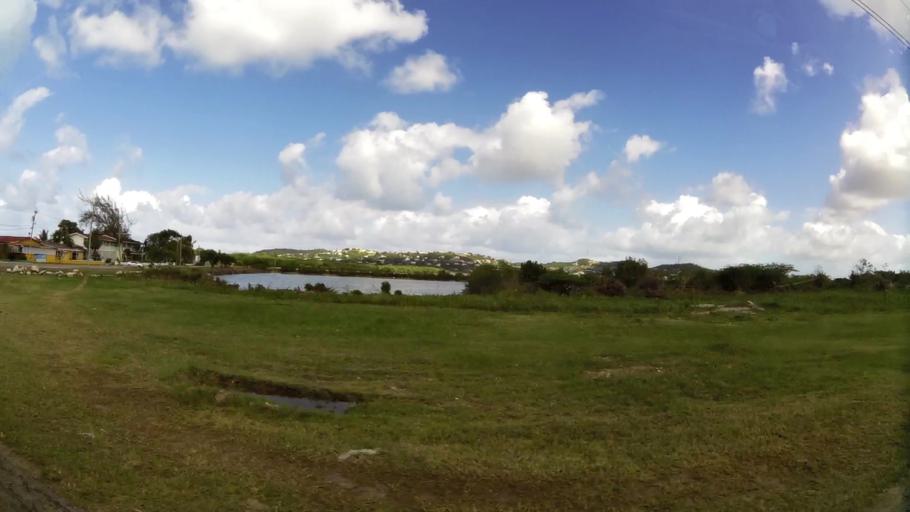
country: AG
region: Saint John
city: Saint John's
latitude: 17.1416
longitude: -61.8584
